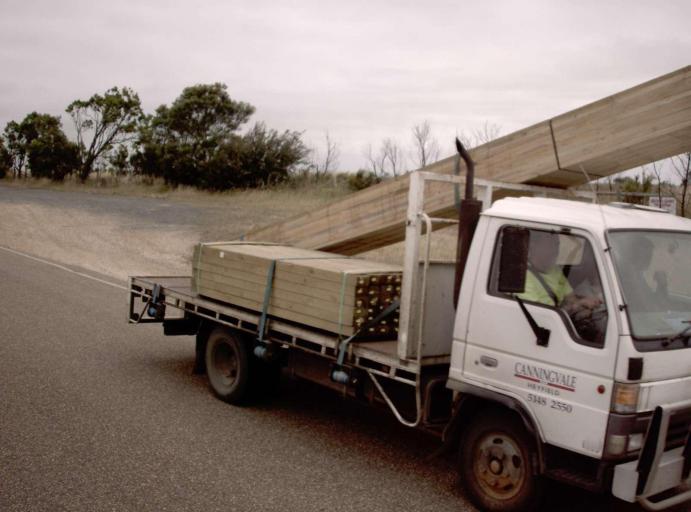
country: AU
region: Victoria
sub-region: Wellington
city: Heyfield
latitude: -38.1279
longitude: 146.7854
